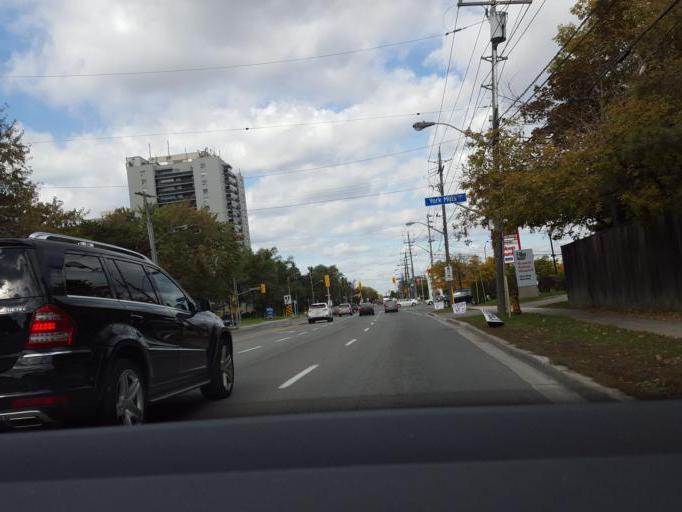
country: CA
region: Ontario
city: Willowdale
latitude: 43.7520
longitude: -79.3596
